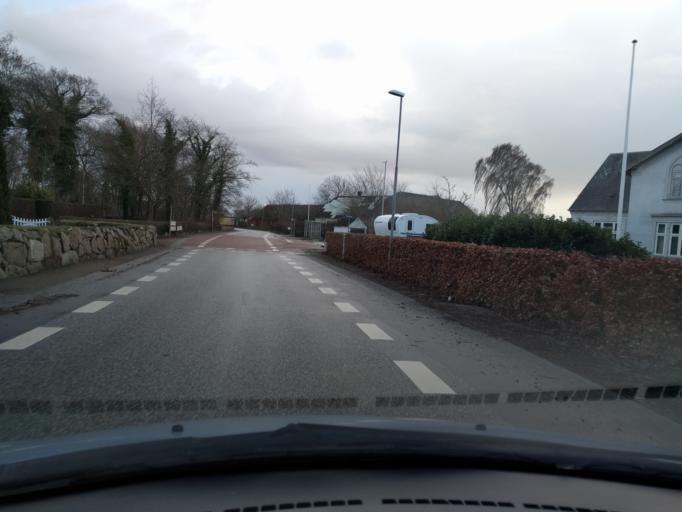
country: DK
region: South Denmark
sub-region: Odense Kommune
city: Bullerup
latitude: 55.3934
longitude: 10.5165
